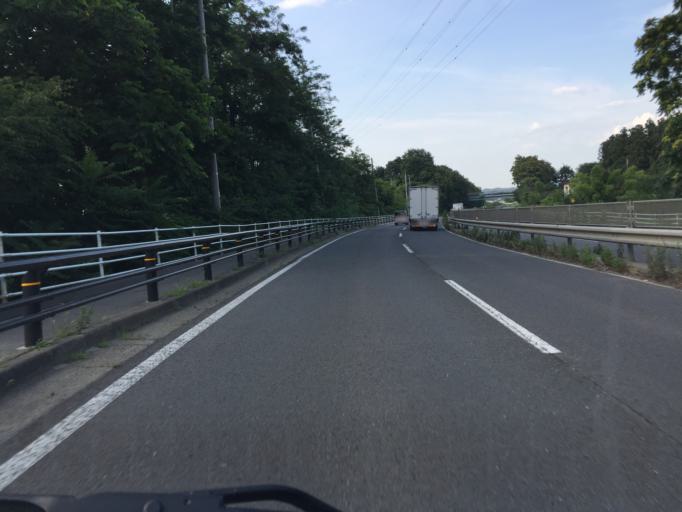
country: JP
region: Fukushima
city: Fukushima-shi
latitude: 37.6999
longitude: 140.4599
